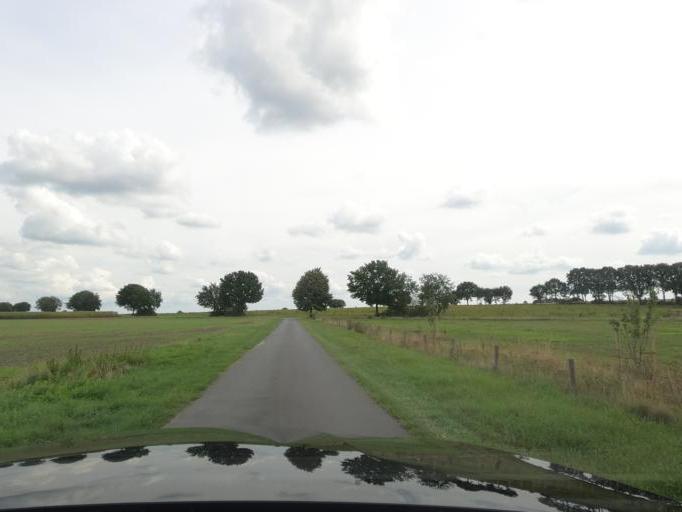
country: DE
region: Lower Saxony
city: Isernhagen Farster Bauerschaft
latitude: 52.5126
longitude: 9.9288
